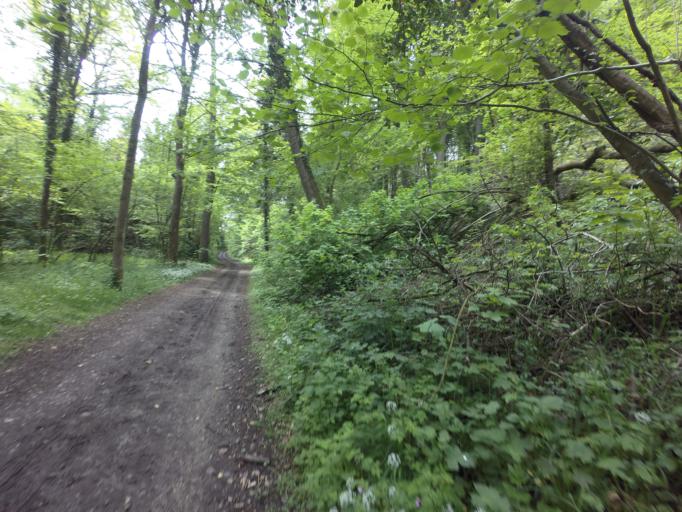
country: NL
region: Limburg
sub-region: Gemeente Maastricht
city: Heer
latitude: 50.8171
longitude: 5.7504
